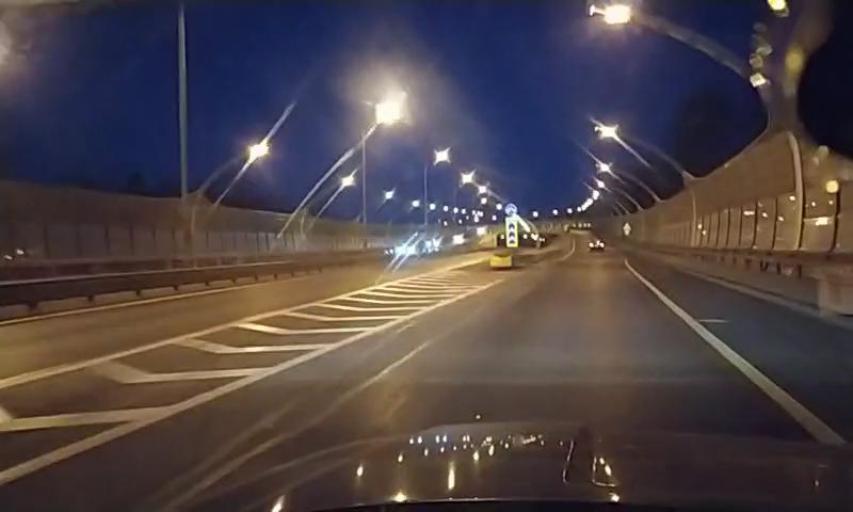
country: RU
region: St.-Petersburg
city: Beloostrov
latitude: 60.1490
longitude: 29.9941
